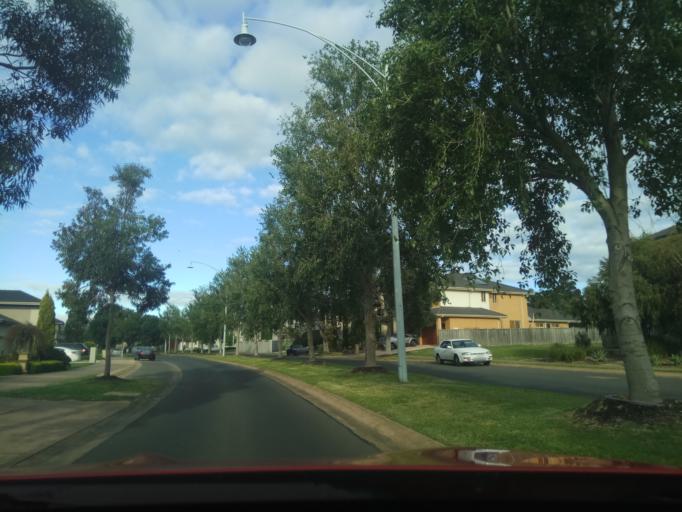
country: AU
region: Victoria
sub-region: Wyndham
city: Point Cook
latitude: -37.9043
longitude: 144.7660
